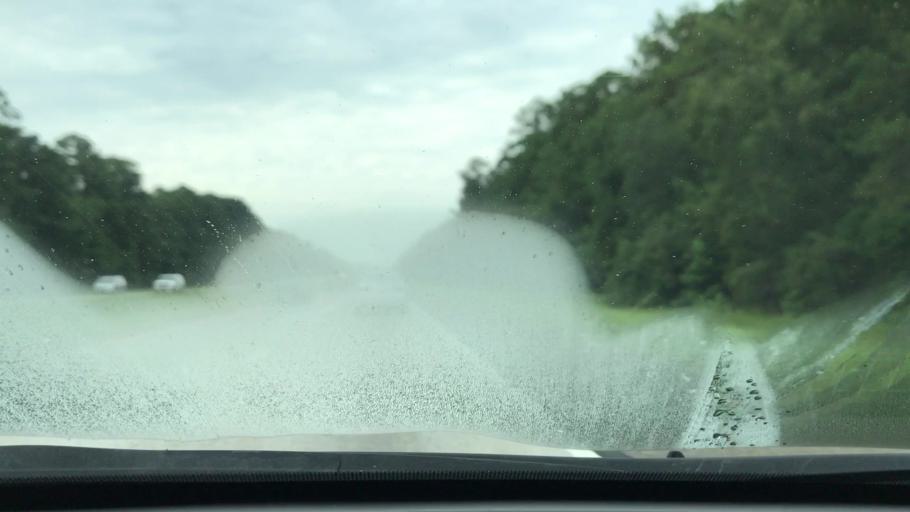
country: US
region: South Carolina
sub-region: Jasper County
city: Hardeeville
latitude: 32.3007
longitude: -81.0619
